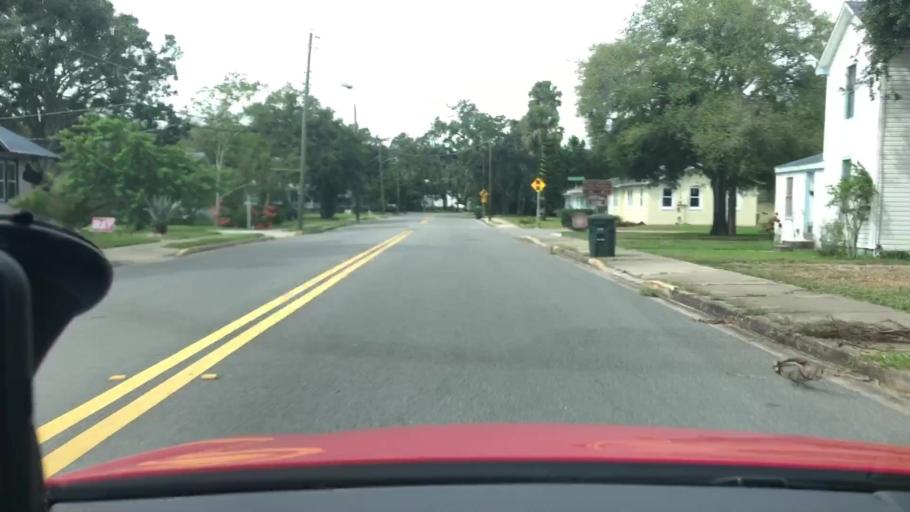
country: US
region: Florida
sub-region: Volusia County
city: Daytona Beach
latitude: 29.1967
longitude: -81.0125
